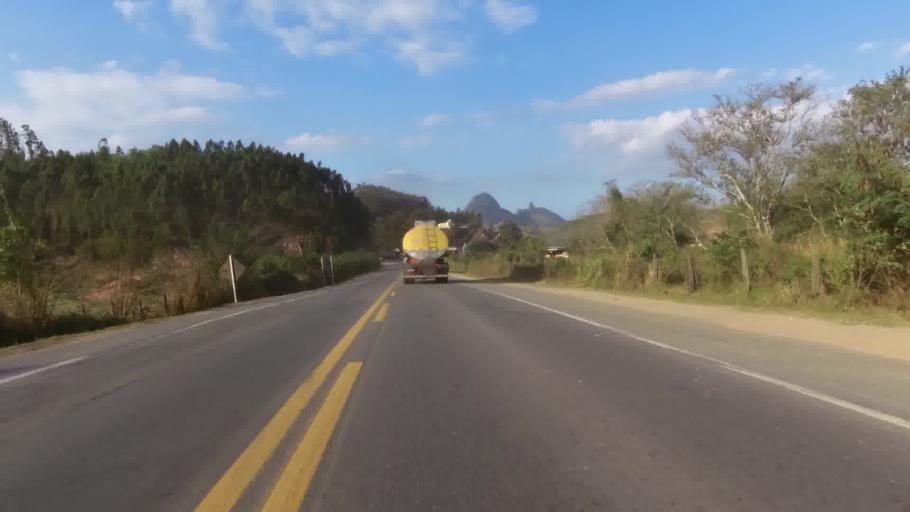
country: BR
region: Espirito Santo
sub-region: Cachoeiro De Itapemirim
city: Cachoeiro de Itapemirim
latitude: -20.8985
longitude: -41.0532
